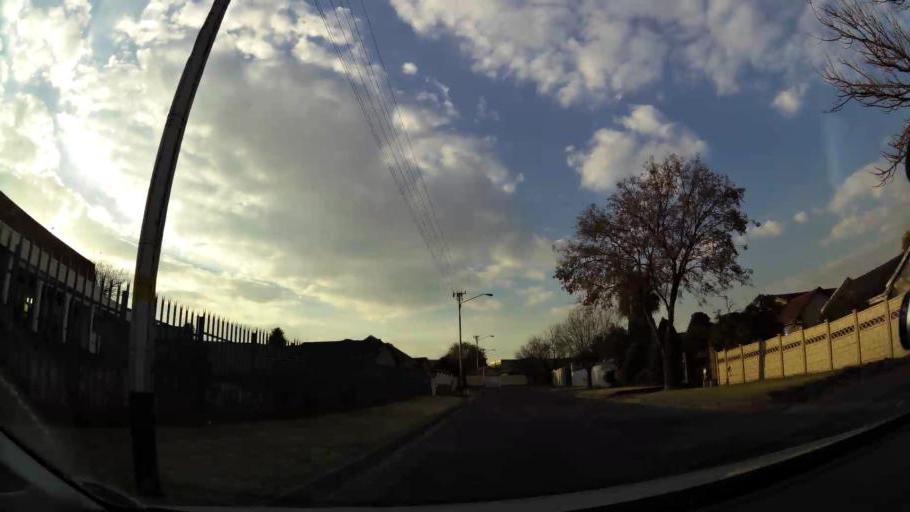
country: ZA
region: Gauteng
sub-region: Ekurhuleni Metropolitan Municipality
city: Germiston
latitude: -26.1814
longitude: 28.1693
